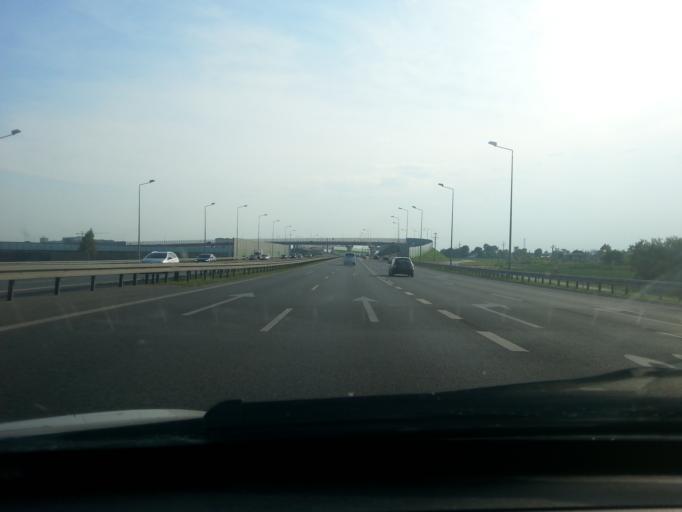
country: PL
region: Masovian Voivodeship
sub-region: Powiat pruszkowski
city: Piastow
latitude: 52.2039
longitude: 20.8482
